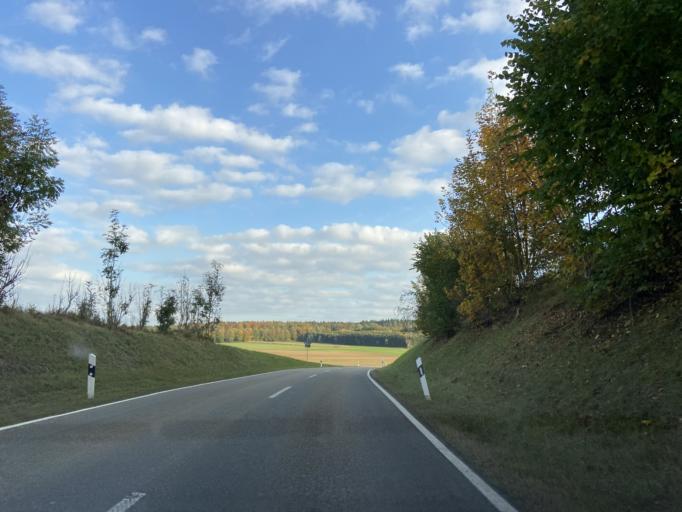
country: DE
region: Baden-Wuerttemberg
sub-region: Tuebingen Region
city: Scheer
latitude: 48.0881
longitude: 9.2852
